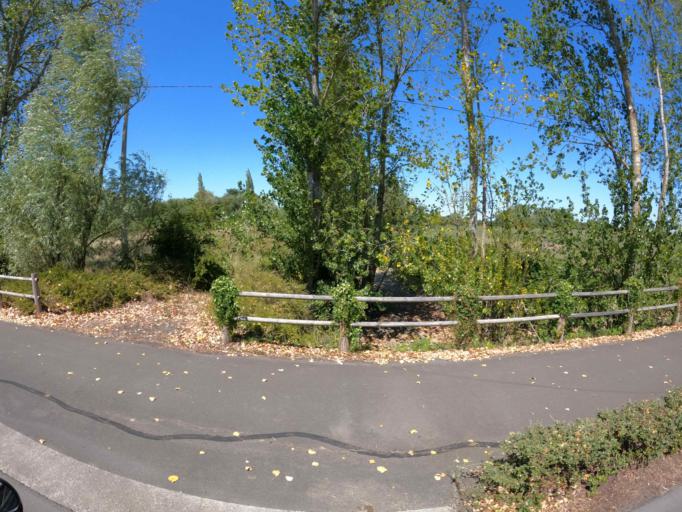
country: FR
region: Pays de la Loire
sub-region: Departement de la Vendee
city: Le Perrier
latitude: 46.8207
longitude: -1.9842
